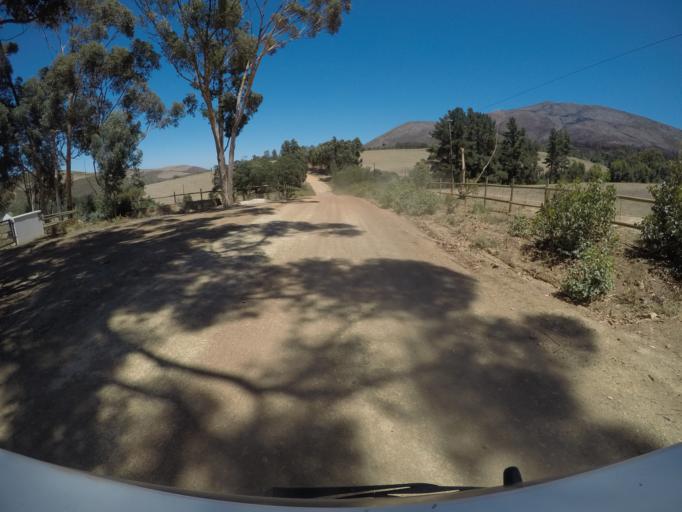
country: ZA
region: Western Cape
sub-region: Overberg District Municipality
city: Caledon
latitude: -34.1941
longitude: 19.2241
